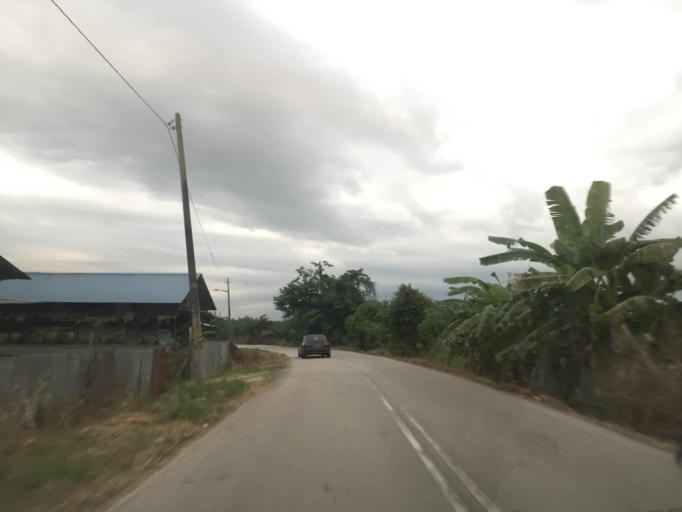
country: MY
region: Penang
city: Tasek Glugor
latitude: 5.5369
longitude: 100.5198
